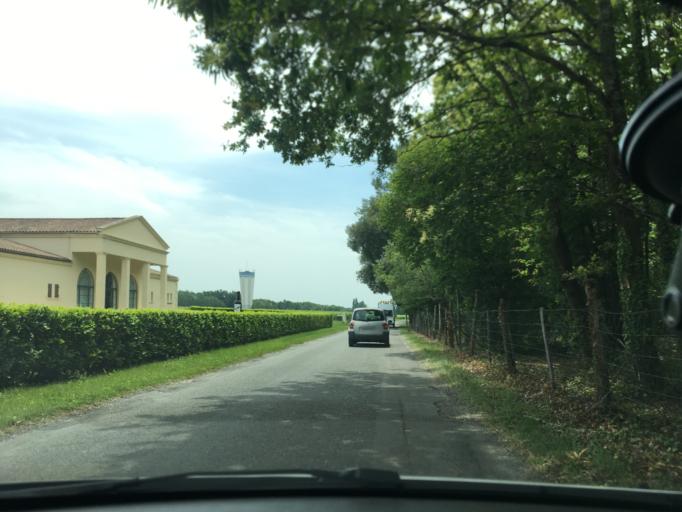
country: FR
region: Aquitaine
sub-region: Departement de la Gironde
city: Castelnau-de-Medoc
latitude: 45.0426
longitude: -0.8045
